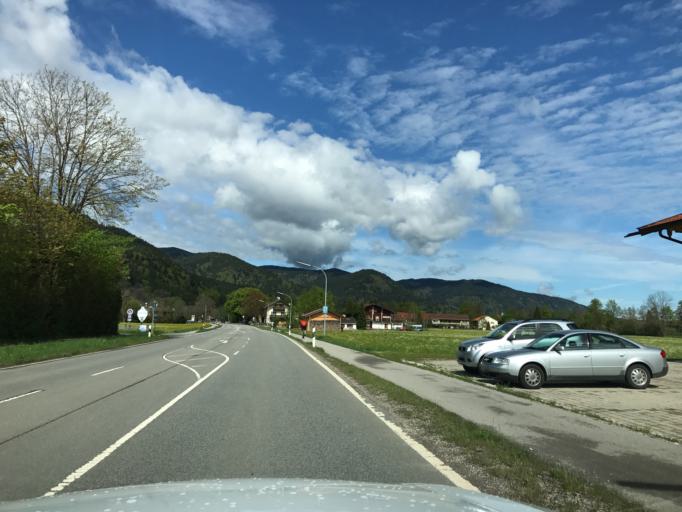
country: DE
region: Bavaria
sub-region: Upper Bavaria
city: Rottach-Egern
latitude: 47.6890
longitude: 11.7515
